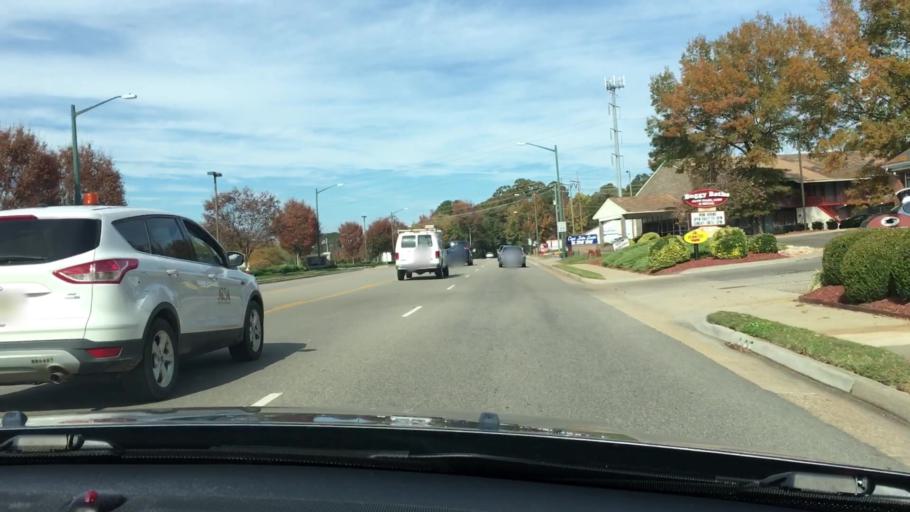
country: US
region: Virginia
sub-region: James City County
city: Williamsburg
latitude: 37.3002
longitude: -76.7275
